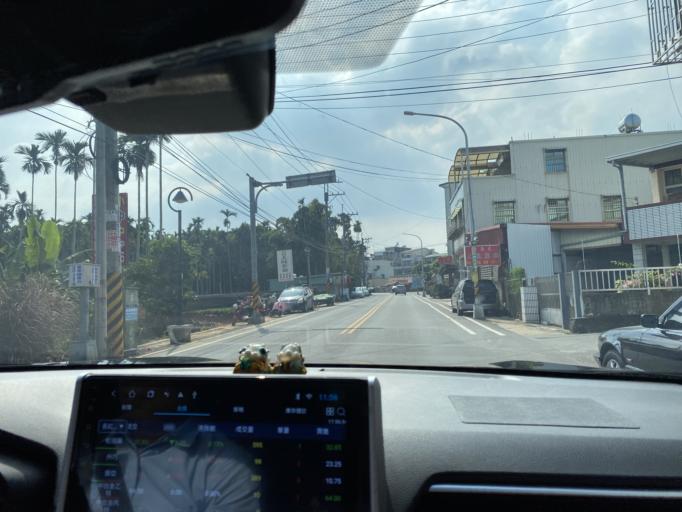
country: TW
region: Taiwan
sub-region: Nantou
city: Nantou
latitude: 23.8420
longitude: 120.6953
